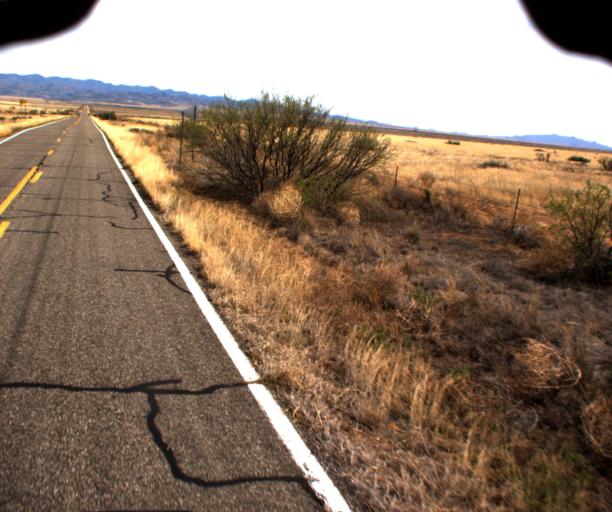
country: US
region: Arizona
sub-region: Cochise County
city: Willcox
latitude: 32.0816
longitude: -109.5224
